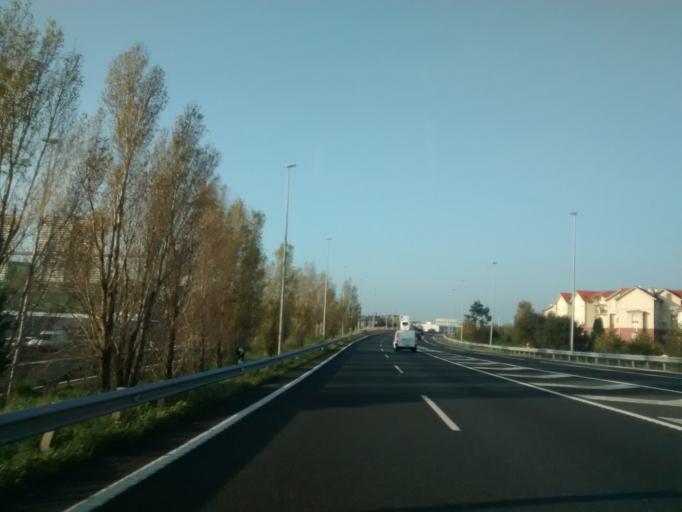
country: ES
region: Cantabria
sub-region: Provincia de Cantabria
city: Santa Cruz de Bezana
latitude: 43.4398
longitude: -3.8955
